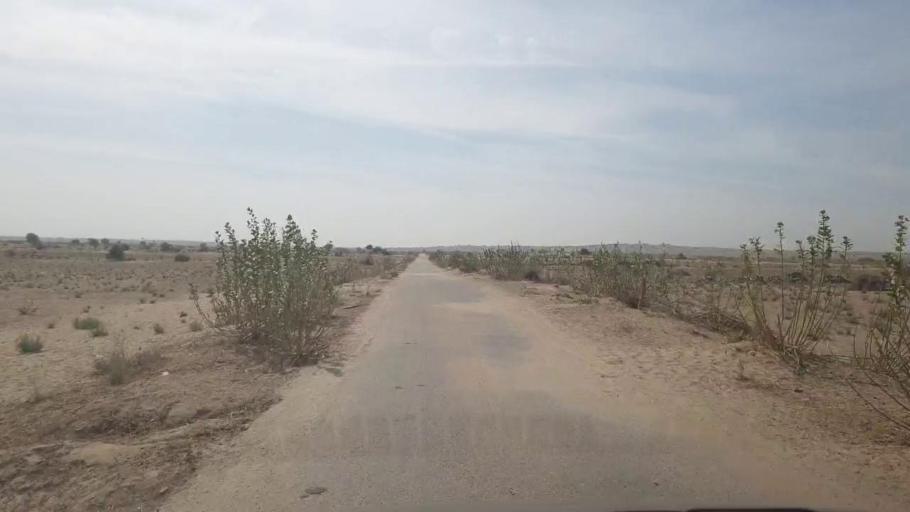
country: PK
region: Sindh
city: Umarkot
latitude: 25.2915
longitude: 69.7281
